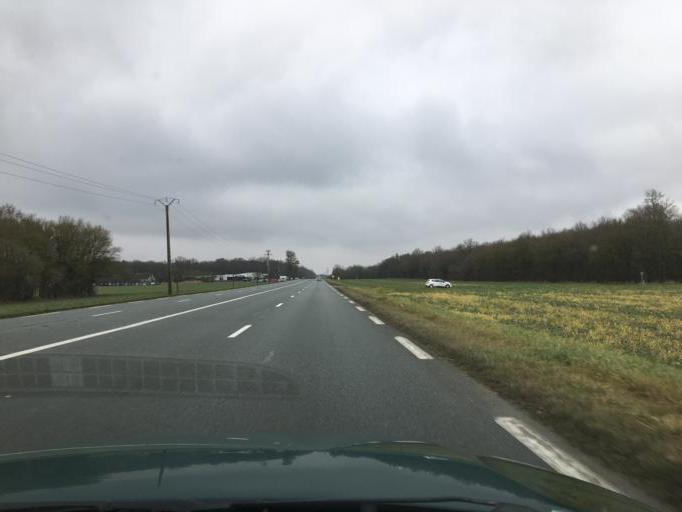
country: FR
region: Centre
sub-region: Departement du Loiret
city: Chevilly
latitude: 47.9981
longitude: 1.8808
